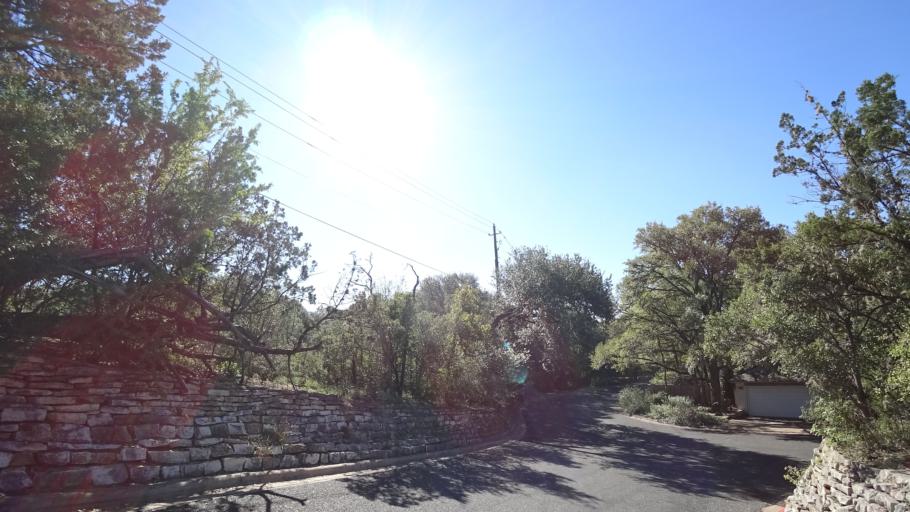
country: US
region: Texas
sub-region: Travis County
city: Austin
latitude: 30.2323
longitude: -97.7098
